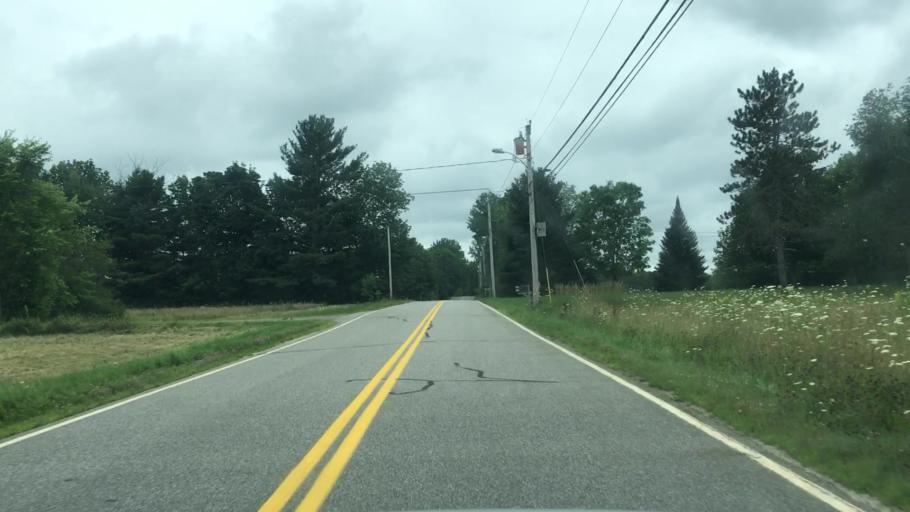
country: US
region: Maine
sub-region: York County
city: Biddeford
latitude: 43.5231
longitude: -70.5110
